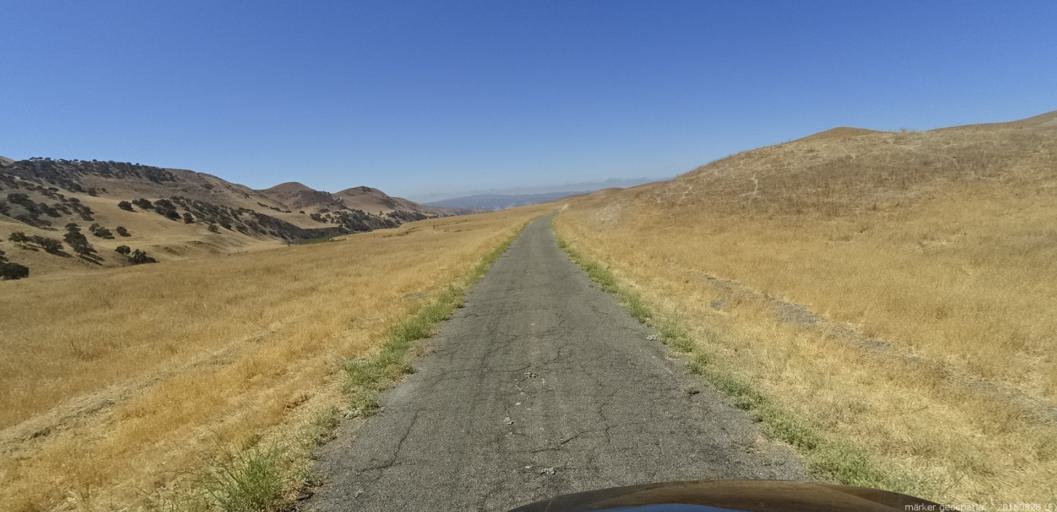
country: US
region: California
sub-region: San Luis Obispo County
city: San Miguel
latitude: 36.0611
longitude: -120.8000
